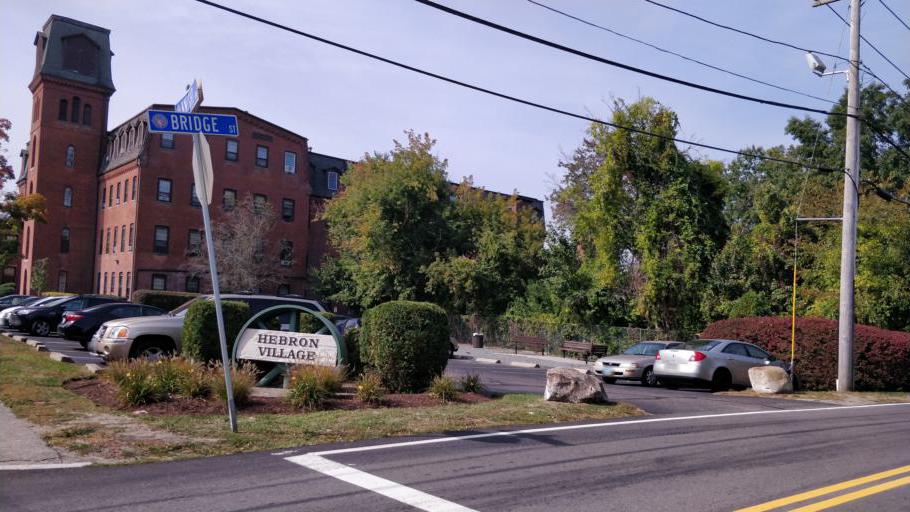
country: US
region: Massachusetts
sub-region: Bristol County
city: North Seekonk
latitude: 41.9050
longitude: -71.3191
